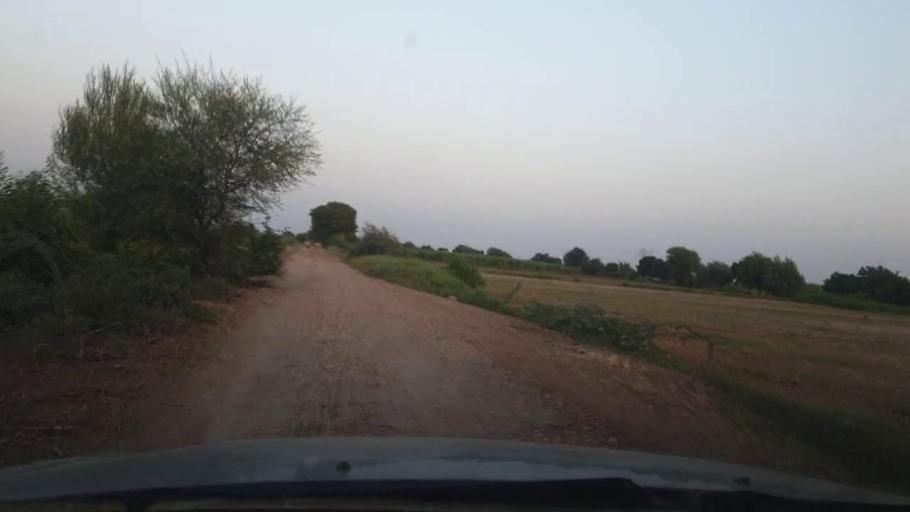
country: PK
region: Sindh
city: Digri
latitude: 25.1113
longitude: 68.9983
